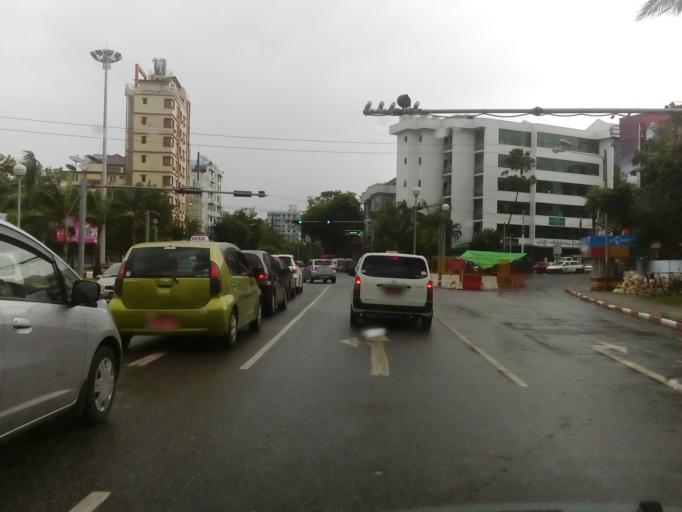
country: MM
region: Yangon
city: Yangon
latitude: 16.8234
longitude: 96.1533
